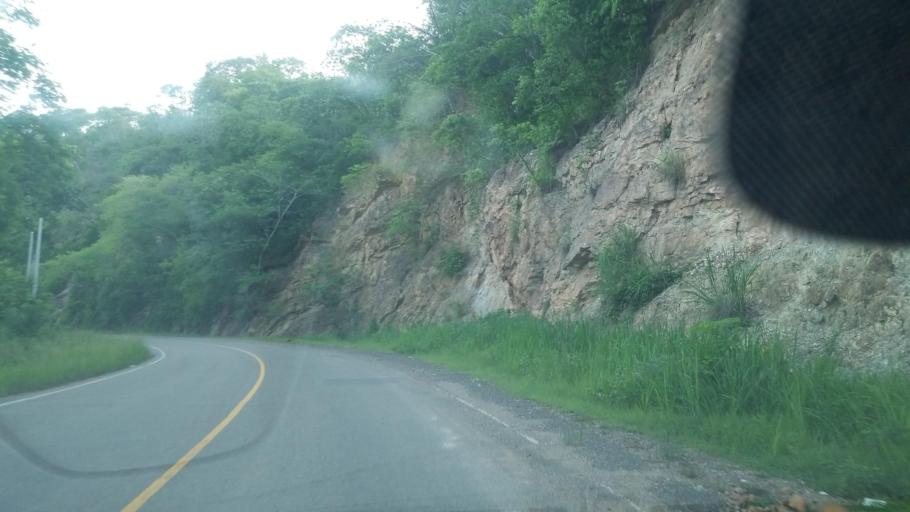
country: HN
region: Santa Barbara
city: Ilama
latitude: 15.0957
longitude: -88.2054
